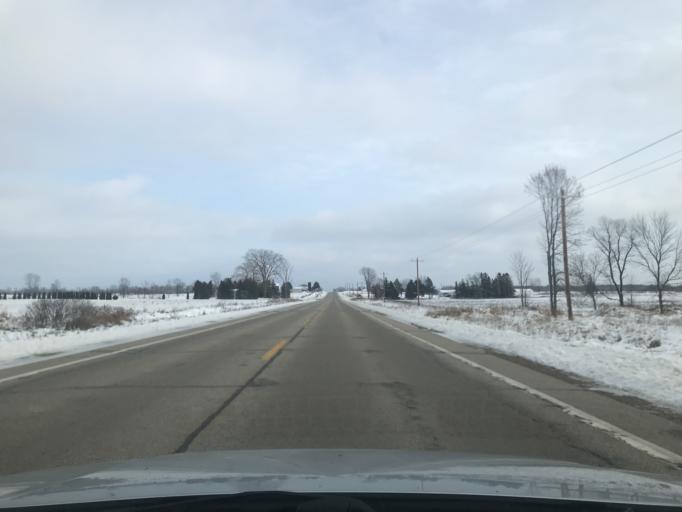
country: US
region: Wisconsin
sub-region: Oconto County
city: Oconto
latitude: 44.8934
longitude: -87.9936
